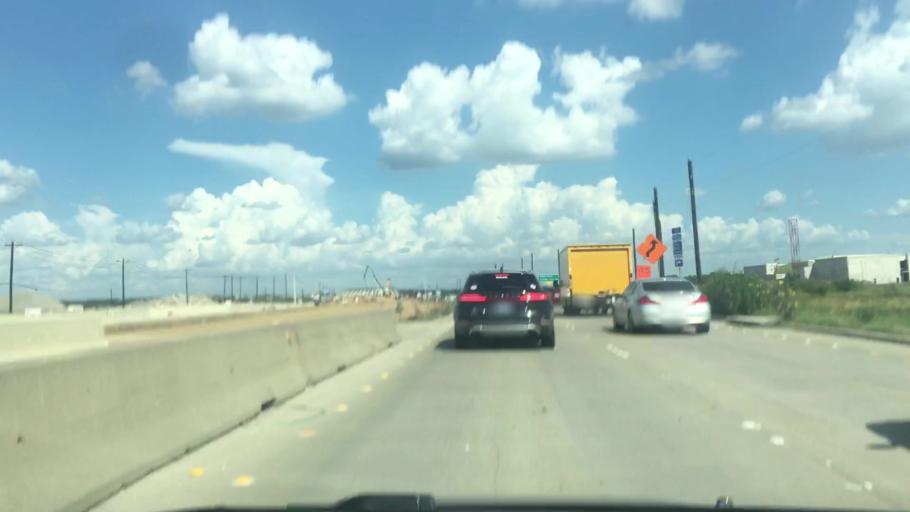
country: US
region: Texas
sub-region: Collin County
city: Prosper
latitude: 33.2190
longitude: -96.8267
